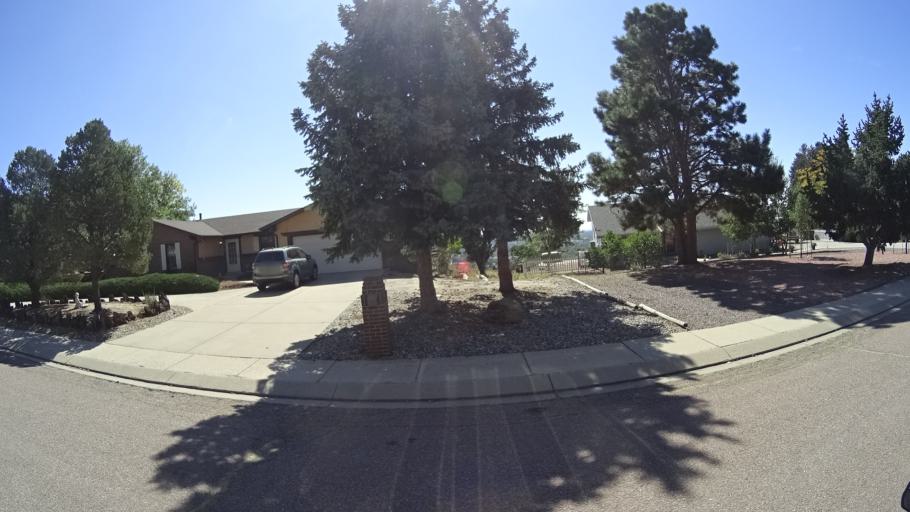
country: US
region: Colorado
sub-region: El Paso County
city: Cimarron Hills
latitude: 38.9131
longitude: -104.7636
